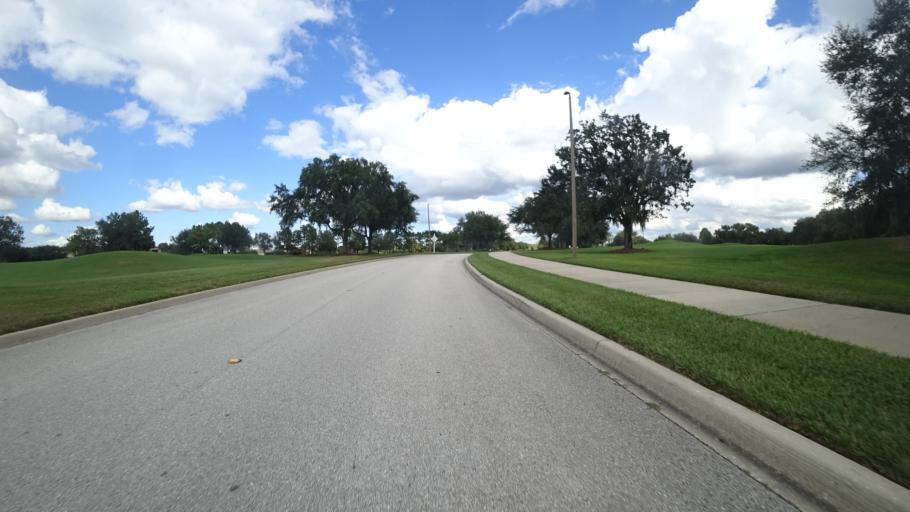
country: US
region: Florida
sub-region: Sarasota County
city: The Meadows
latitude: 27.4059
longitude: -82.4188
